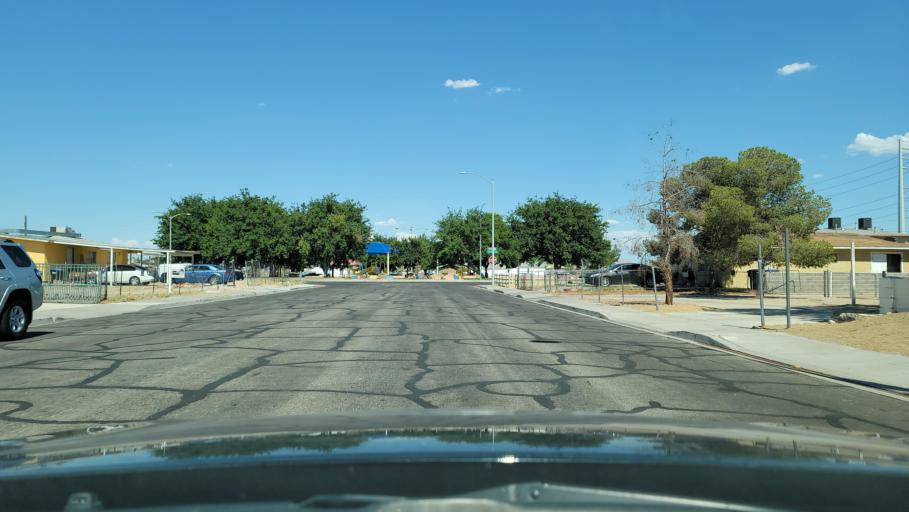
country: US
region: Nevada
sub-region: Clark County
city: Las Vegas
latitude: 36.1994
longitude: -115.1578
